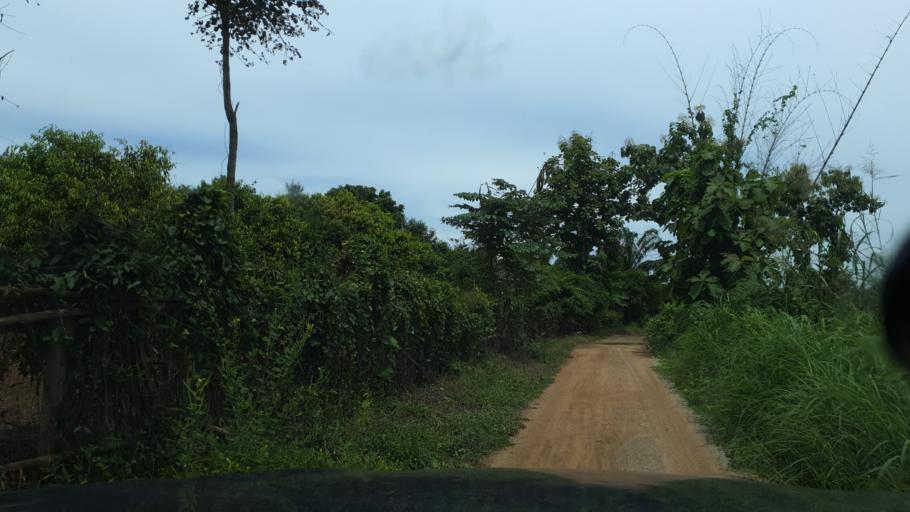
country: TH
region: Sukhothai
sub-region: Amphoe Si Satchanalai
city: Si Satchanalai
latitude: 17.6653
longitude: 99.6889
